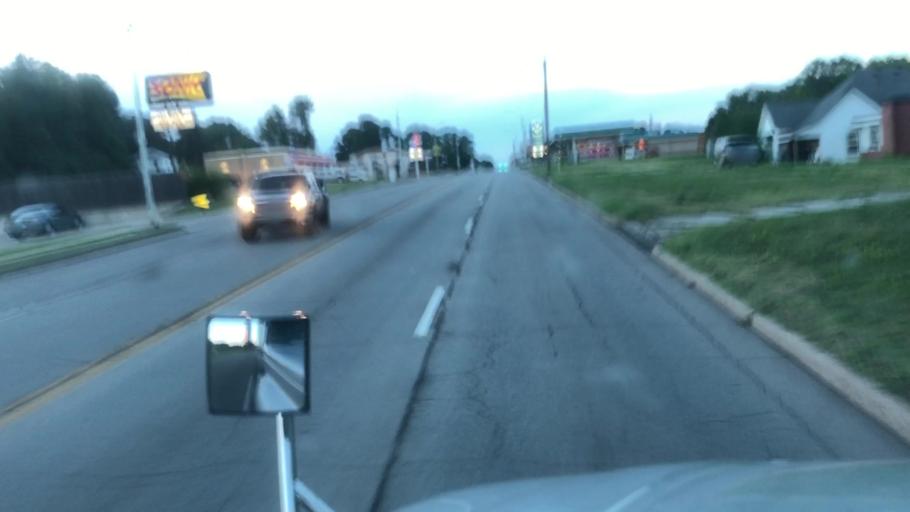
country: US
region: Oklahoma
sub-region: Kay County
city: Ponca City
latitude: 36.6976
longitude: -97.0672
